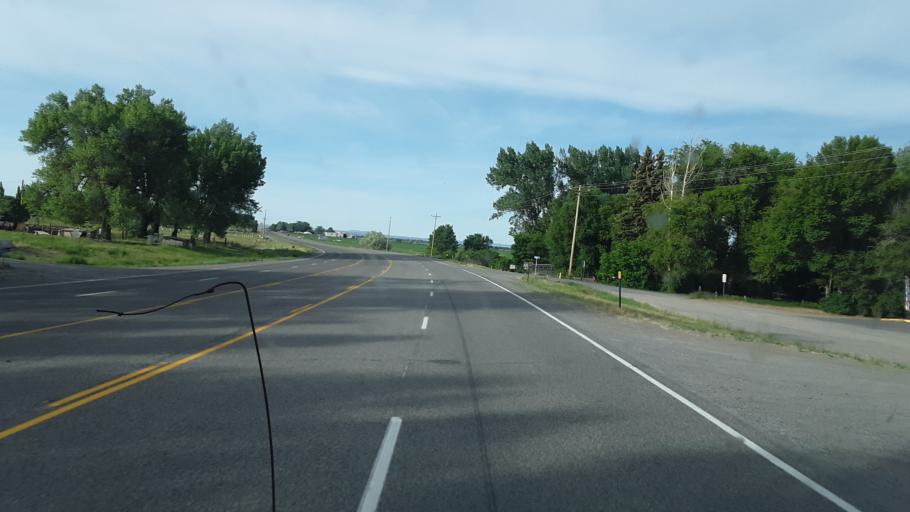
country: US
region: Wyoming
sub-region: Fremont County
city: Riverton
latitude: 43.0805
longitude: -108.3806
